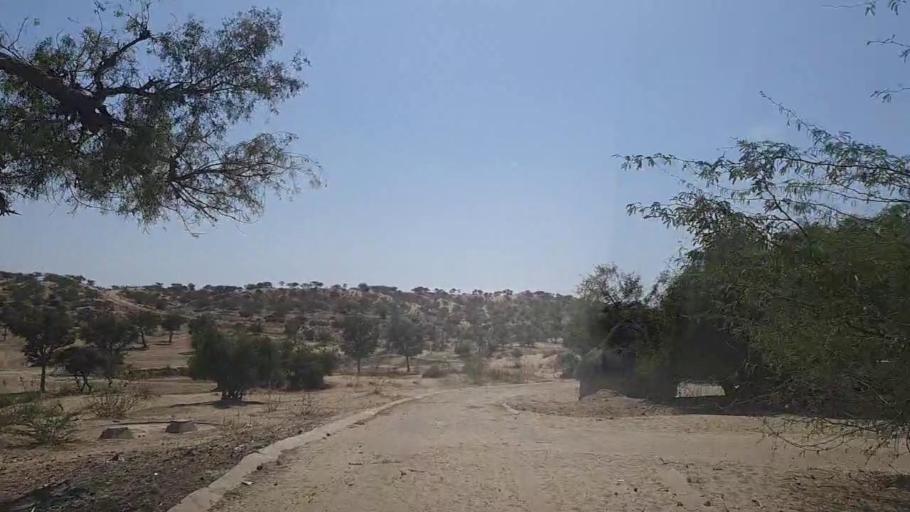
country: PK
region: Sindh
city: Mithi
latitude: 24.8697
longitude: 69.6617
